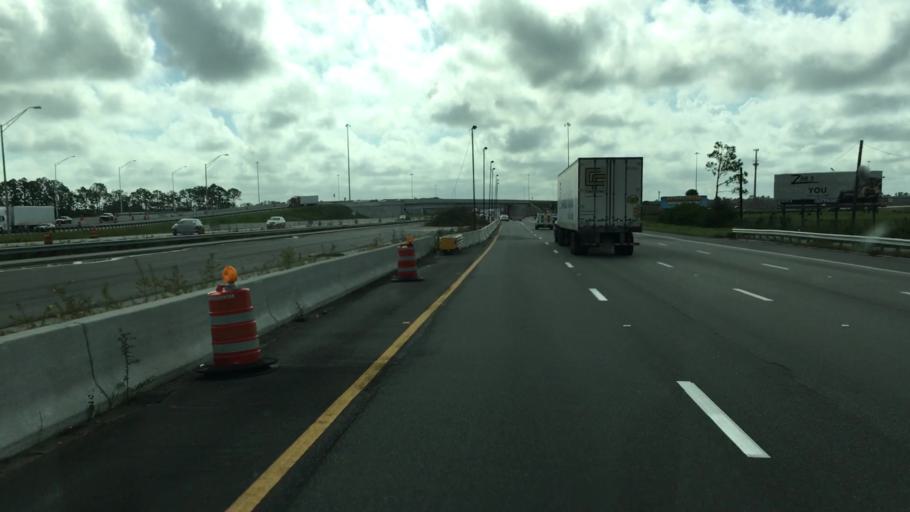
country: US
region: Florida
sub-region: Volusia County
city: South Daytona
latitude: 29.1611
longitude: -81.0793
